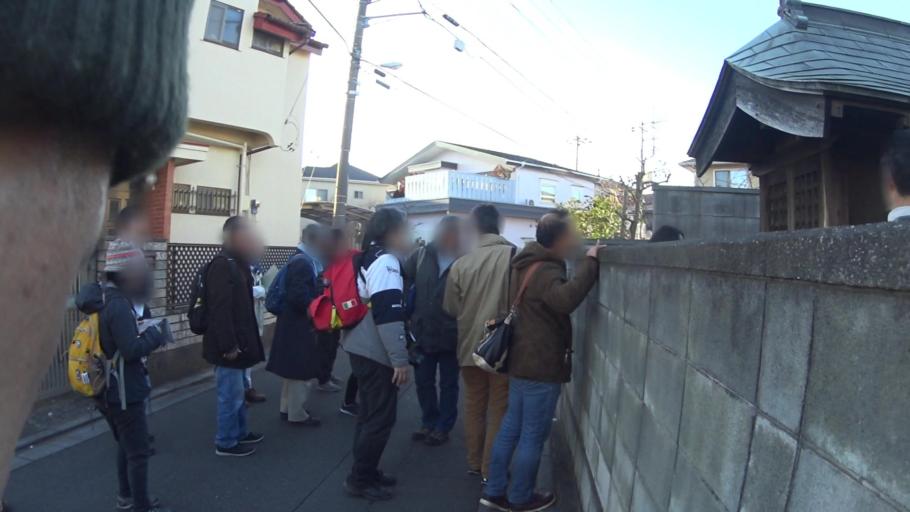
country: JP
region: Saitama
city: Shimotoda
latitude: 35.8501
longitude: 139.6895
